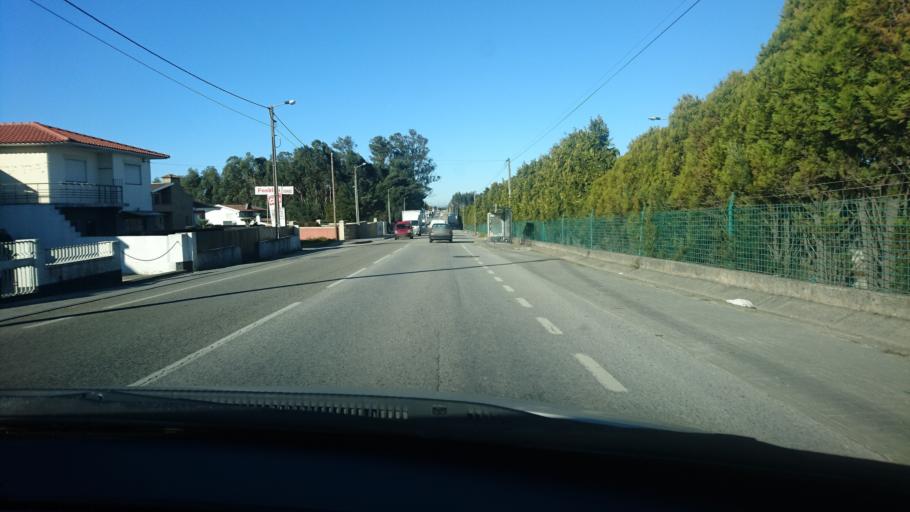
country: PT
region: Aveiro
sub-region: Santa Maria da Feira
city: Sao Joao de Ver
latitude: 40.9552
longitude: -8.5273
